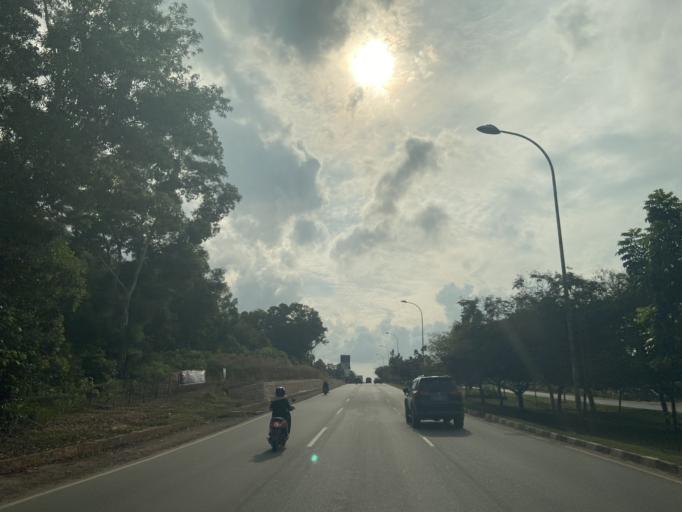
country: SG
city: Singapore
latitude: 1.0998
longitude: 104.0451
